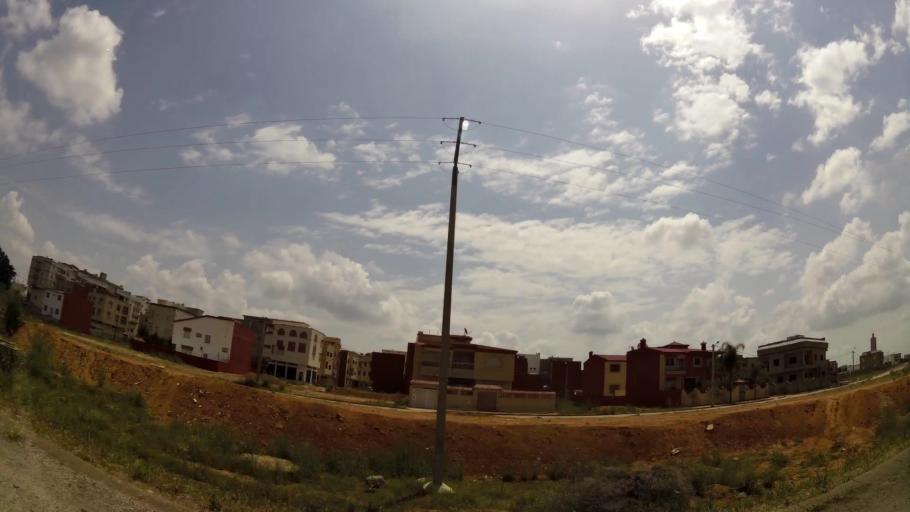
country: MA
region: Gharb-Chrarda-Beni Hssen
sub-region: Kenitra Province
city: Kenitra
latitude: 34.0112
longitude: -6.5404
